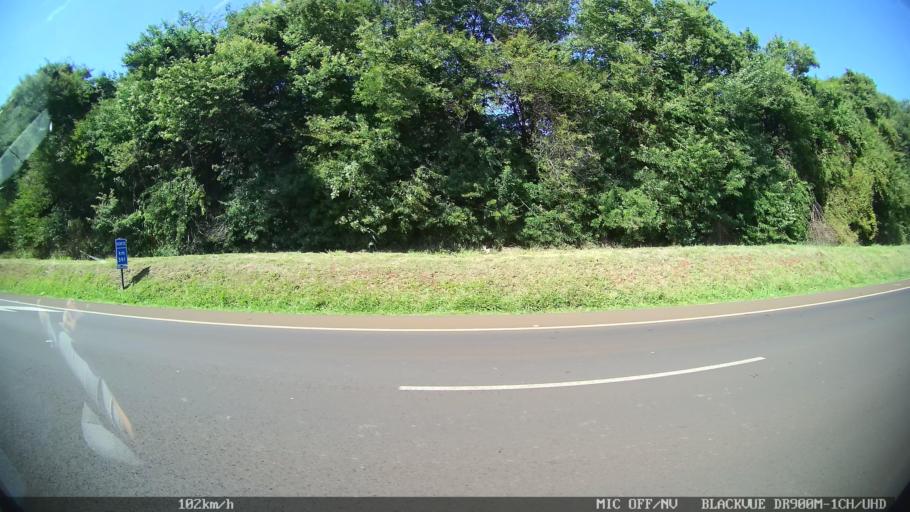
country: BR
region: Sao Paulo
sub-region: Franca
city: Franca
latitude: -20.5869
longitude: -47.4350
